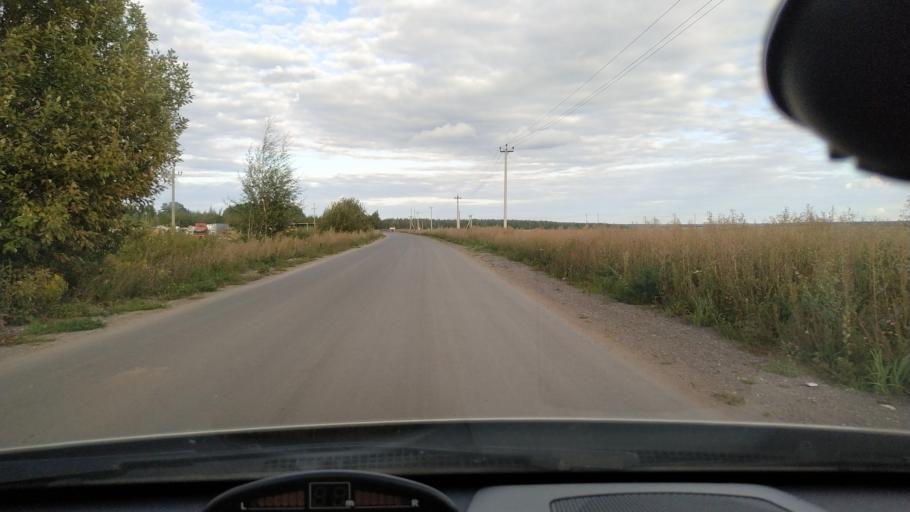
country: RU
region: Rjazan
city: Polyany
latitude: 54.5767
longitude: 39.8467
